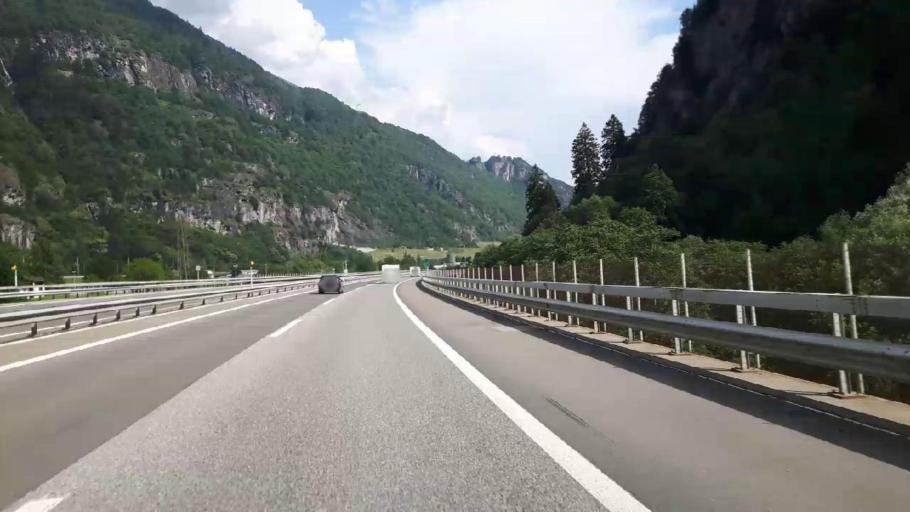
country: CH
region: Ticino
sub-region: Leventina District
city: Faido
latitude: 46.4670
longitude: 8.8179
